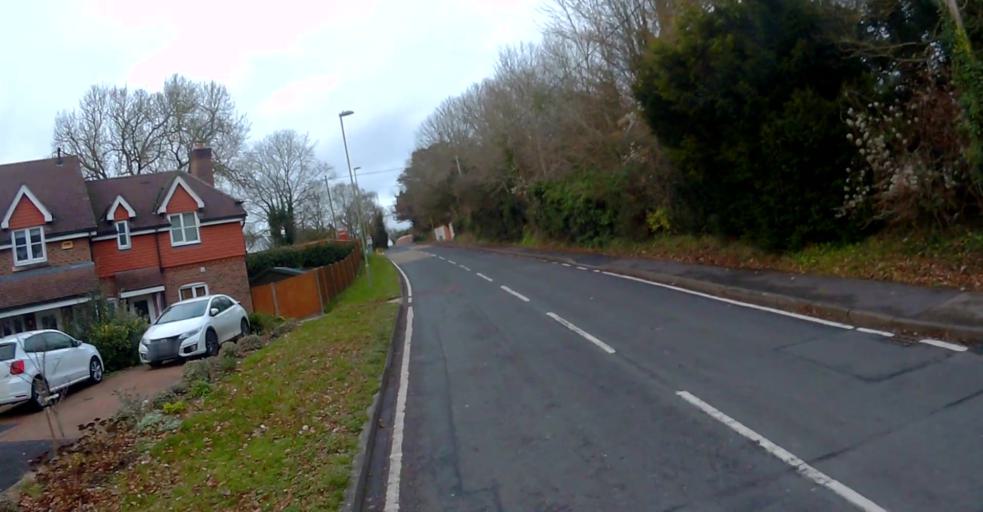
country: GB
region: England
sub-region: Hampshire
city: Overton
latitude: 51.2517
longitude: -1.2640
